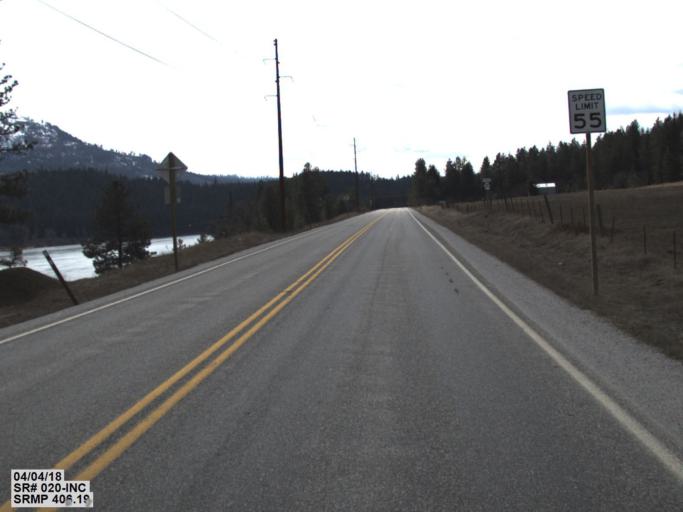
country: US
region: Washington
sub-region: Pend Oreille County
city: Newport
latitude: 48.4949
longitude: -117.2686
